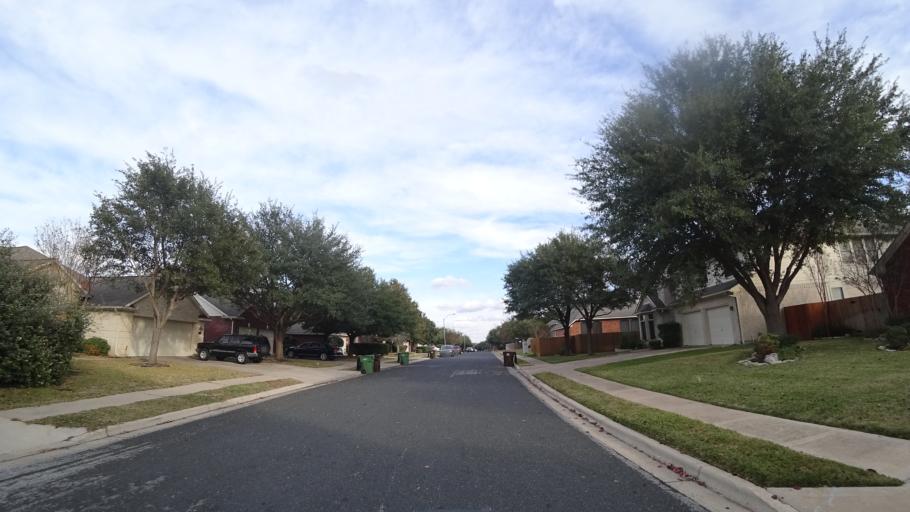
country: US
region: Texas
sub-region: Williamson County
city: Brushy Creek
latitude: 30.5190
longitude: -97.7317
